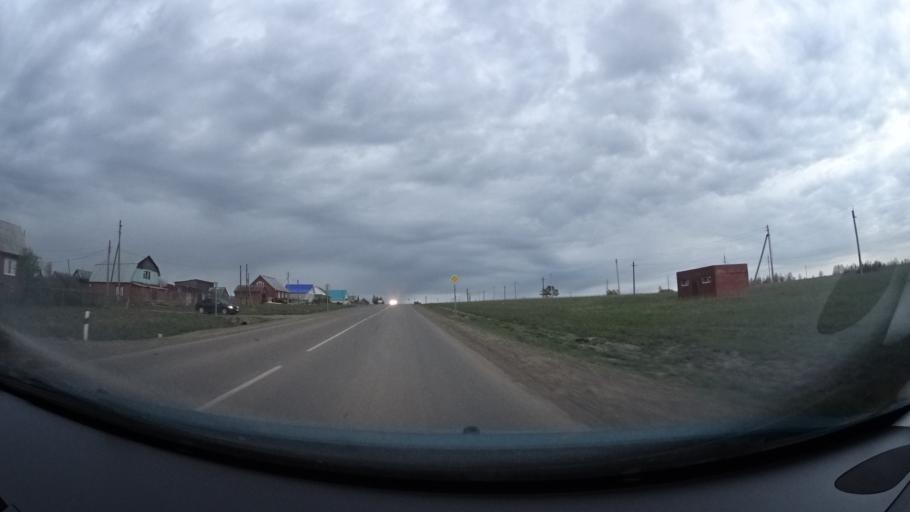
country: RU
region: Perm
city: Kuyeda
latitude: 56.4197
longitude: 55.5865
